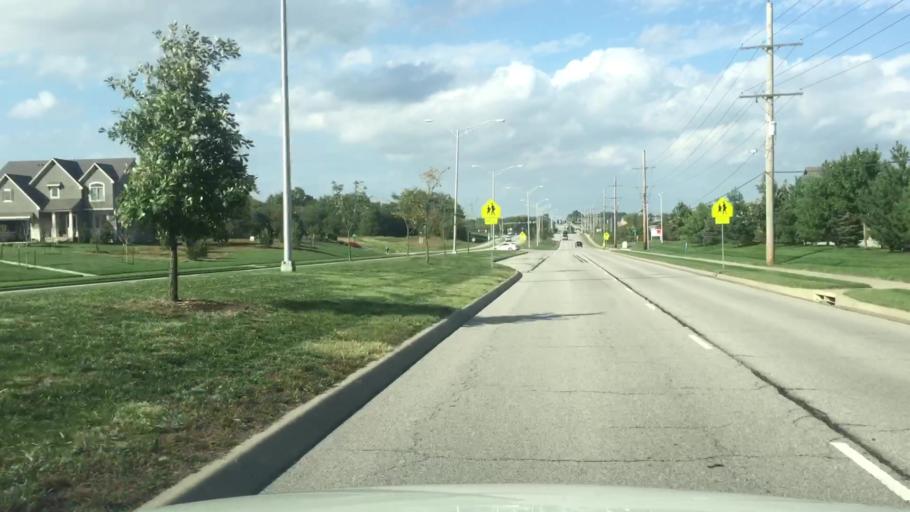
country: US
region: Kansas
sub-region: Johnson County
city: Lenexa
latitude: 38.8294
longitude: -94.6863
